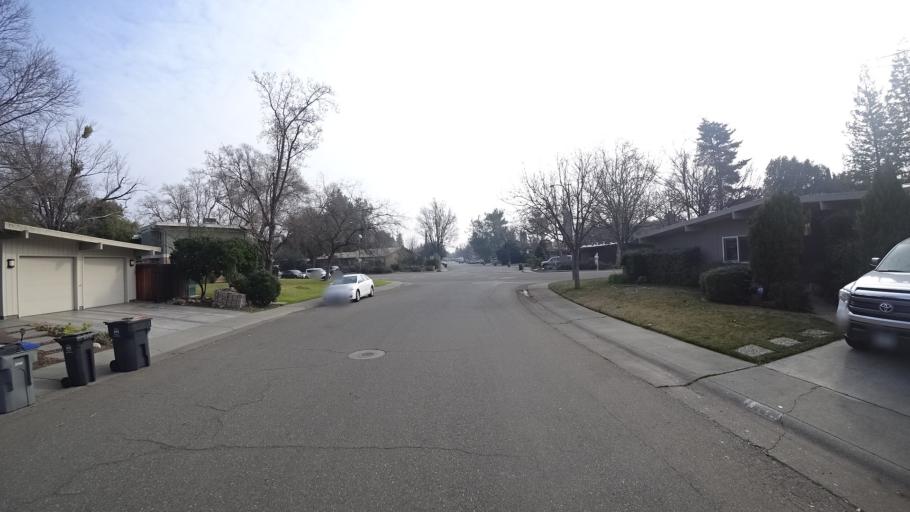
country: US
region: California
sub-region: Yolo County
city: Davis
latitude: 38.5587
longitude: -121.7652
